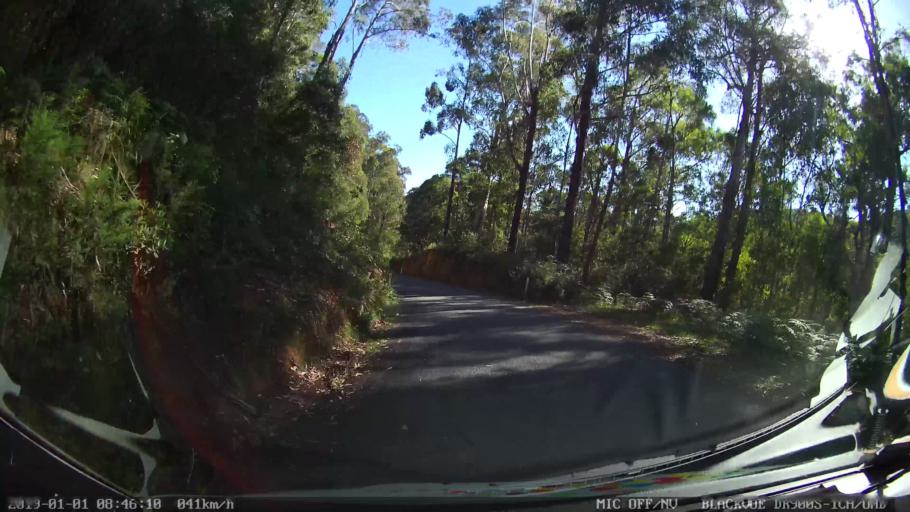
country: AU
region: New South Wales
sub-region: Snowy River
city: Jindabyne
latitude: -36.3016
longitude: 148.1922
